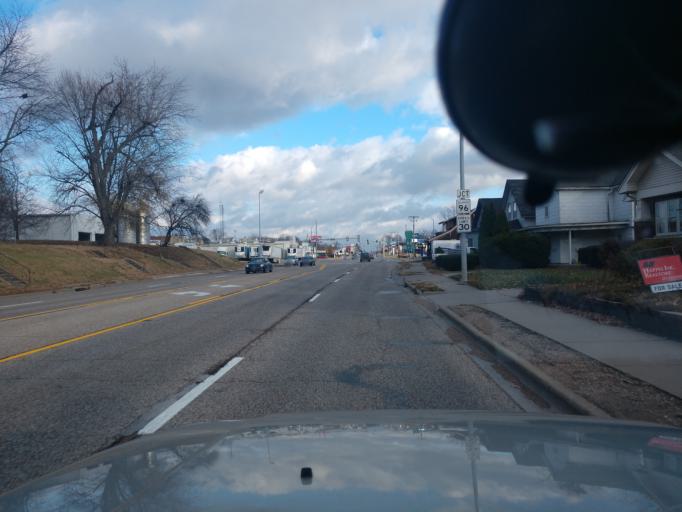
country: US
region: Illinois
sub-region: Adams County
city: Quincy
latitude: 39.9354
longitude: -91.3796
